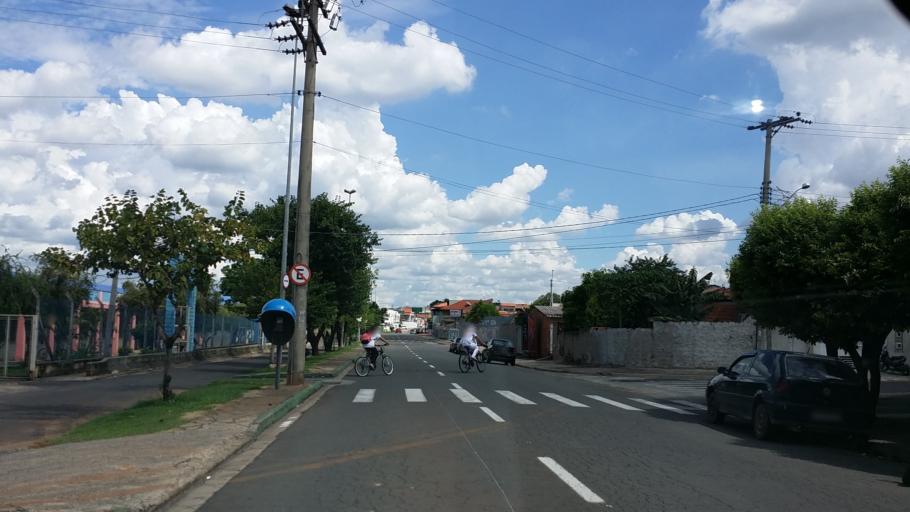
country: BR
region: Sao Paulo
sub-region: Indaiatuba
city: Indaiatuba
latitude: -23.1215
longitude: -47.2339
